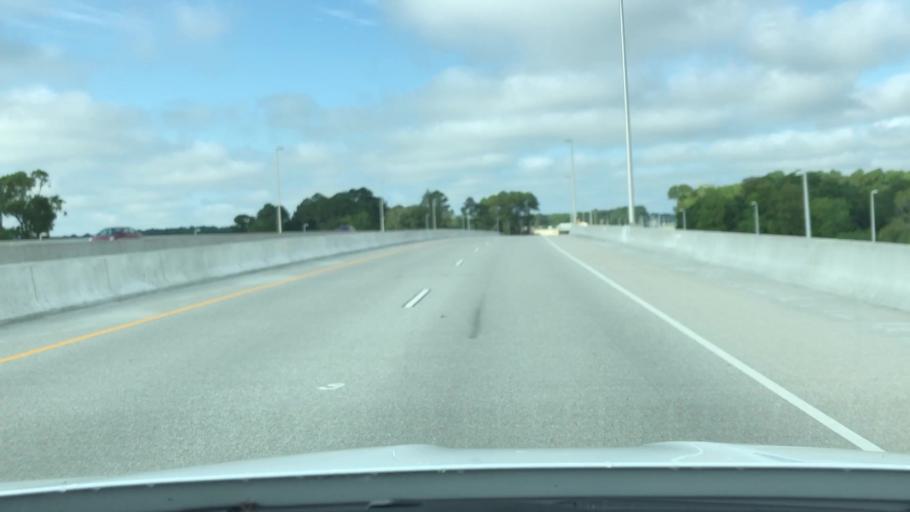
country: US
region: Virginia
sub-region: City of Chesapeake
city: Chesapeake
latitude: 36.7283
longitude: -76.3019
